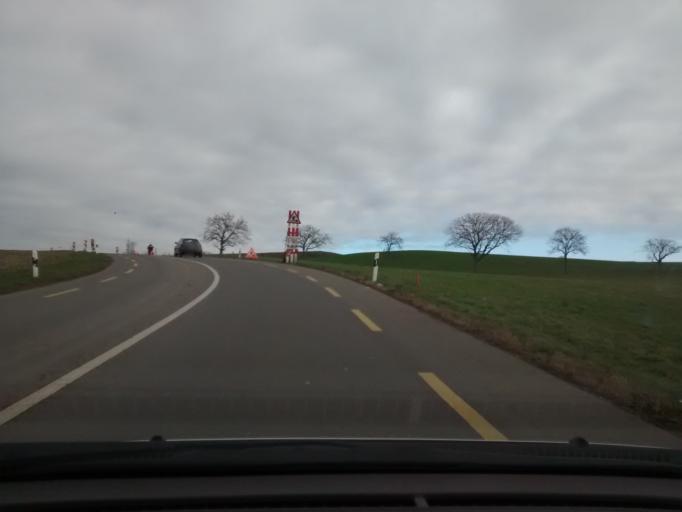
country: CH
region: Vaud
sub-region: Lausanne District
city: Blecherette
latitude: 46.5481
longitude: 6.6132
